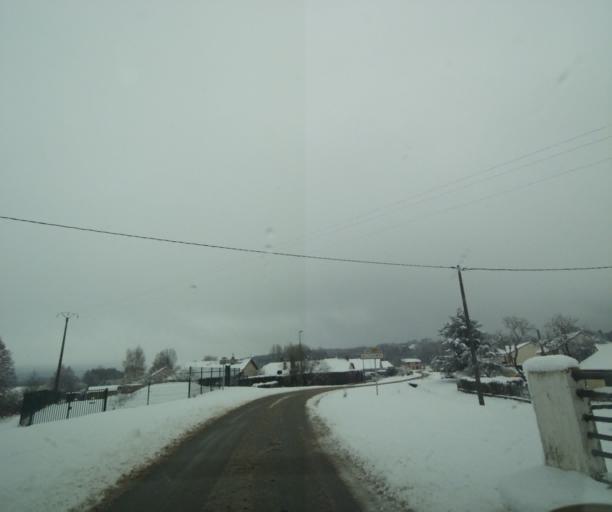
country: FR
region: Champagne-Ardenne
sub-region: Departement de la Haute-Marne
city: Wassy
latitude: 48.5642
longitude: 4.8956
